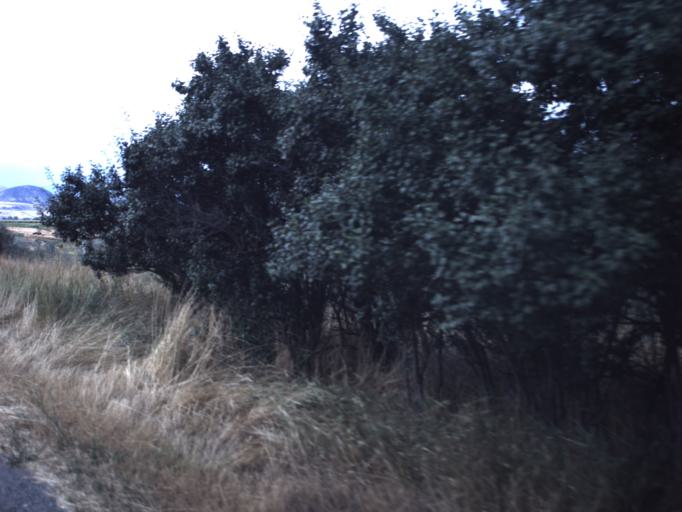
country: US
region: Utah
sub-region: Cache County
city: Lewiston
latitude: 41.9159
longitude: -111.9320
